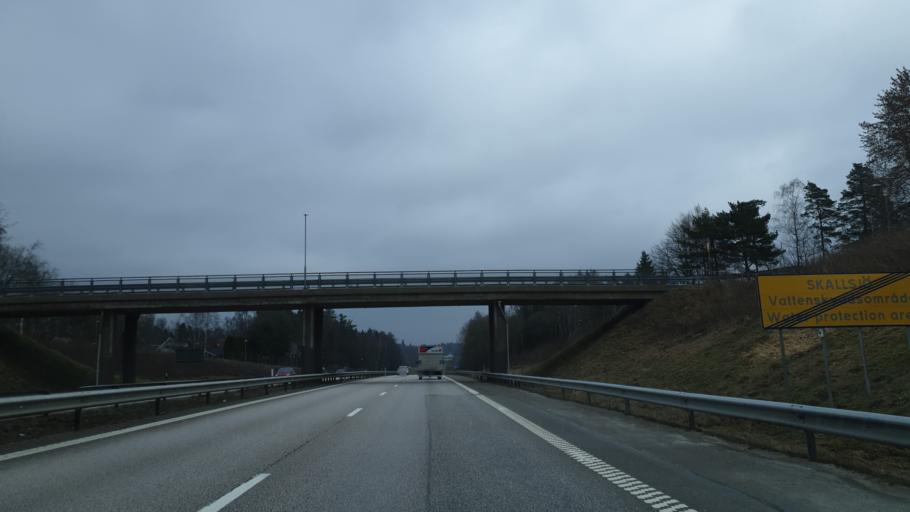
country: SE
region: Vaestra Goetaland
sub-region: Lerums Kommun
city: Stenkullen
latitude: 57.7972
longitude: 12.3561
